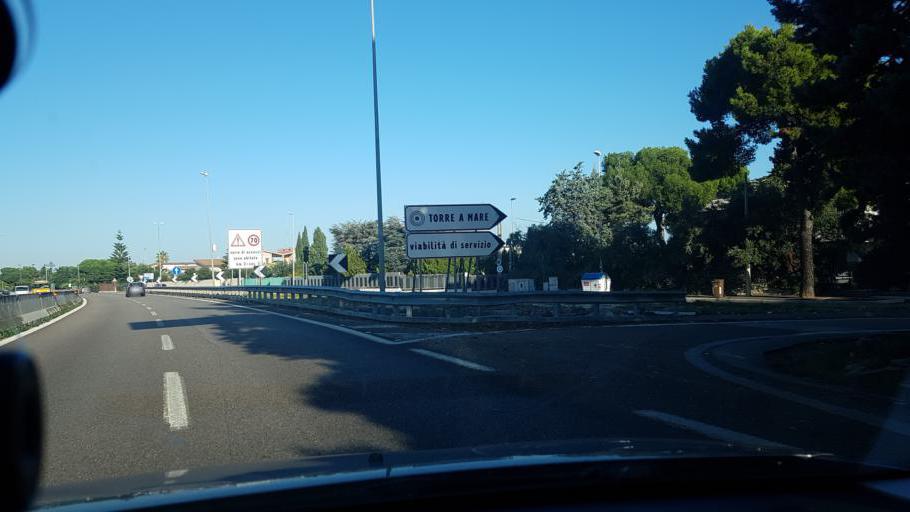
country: IT
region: Apulia
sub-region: Provincia di Bari
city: Parco Scizzo-Parchitello
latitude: 41.0866
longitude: 16.9891
